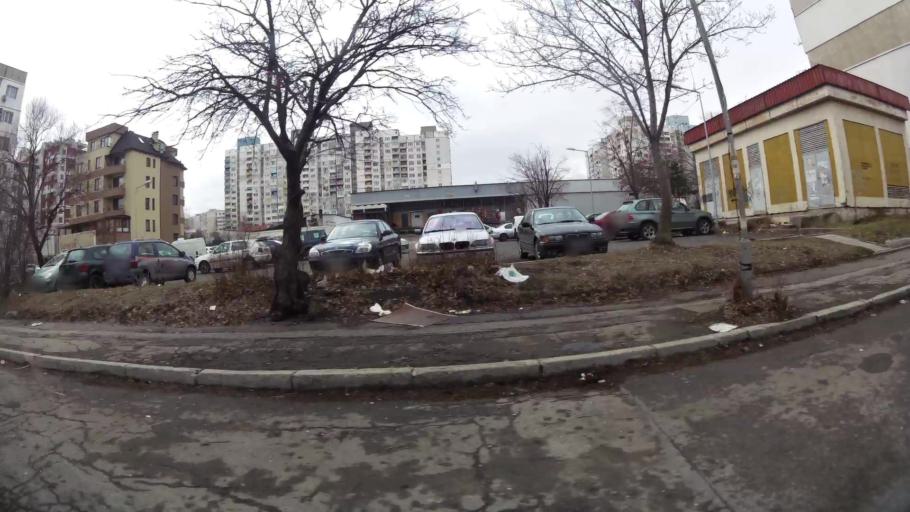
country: BG
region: Sofiya
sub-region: Obshtina Bozhurishte
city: Bozhurishte
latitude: 42.7250
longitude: 23.2478
